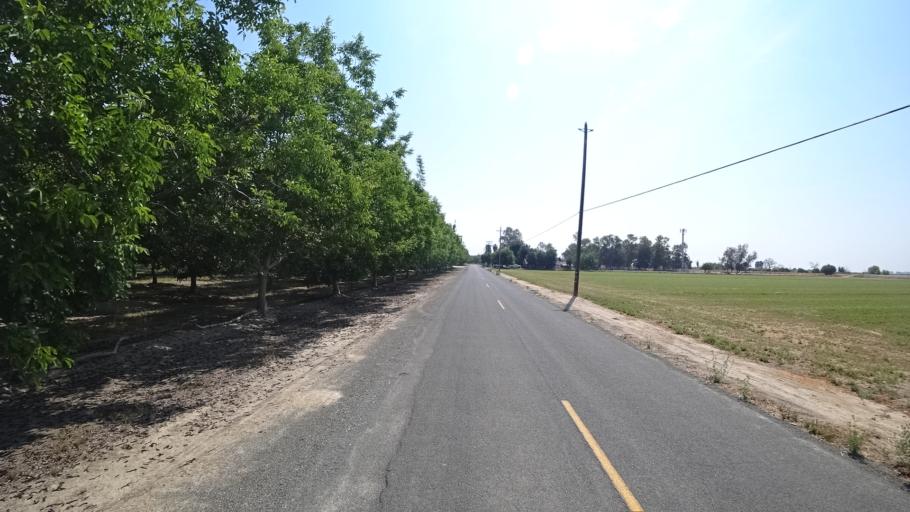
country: US
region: California
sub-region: Fresno County
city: Laton
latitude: 36.3948
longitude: -119.7664
